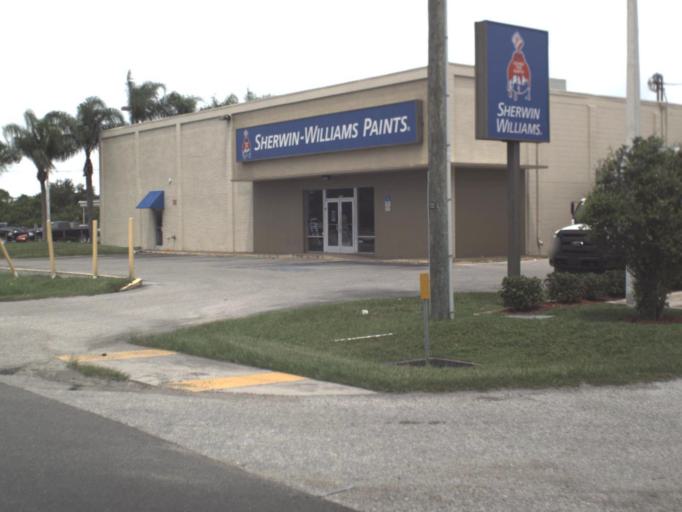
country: US
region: Florida
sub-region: Hillsborough County
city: Egypt Lake-Leto
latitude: 27.9963
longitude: -82.5245
